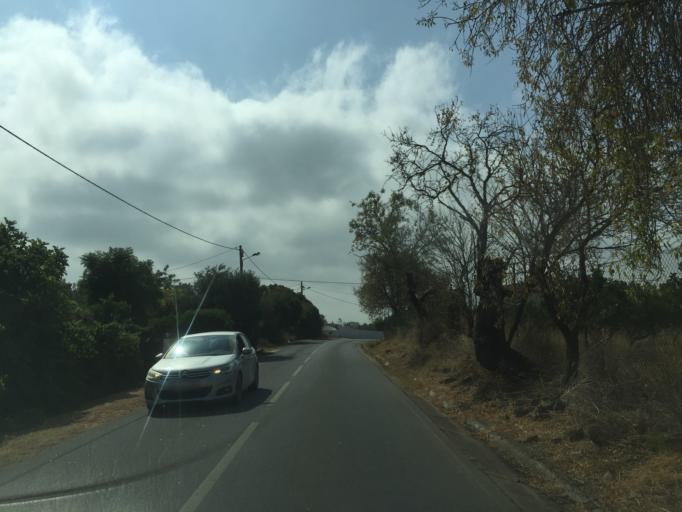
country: PT
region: Faro
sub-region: Olhao
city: Olhao
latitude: 37.0772
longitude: -7.8900
